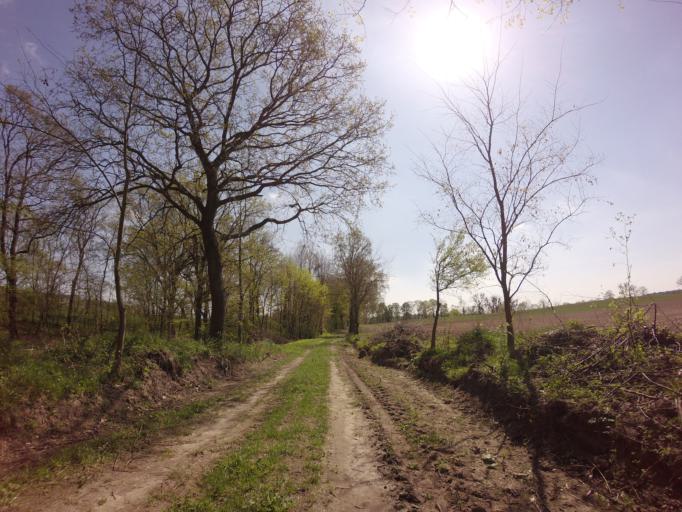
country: PL
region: West Pomeranian Voivodeship
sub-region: Powiat stargardzki
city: Suchan
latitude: 53.1894
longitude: 15.3154
